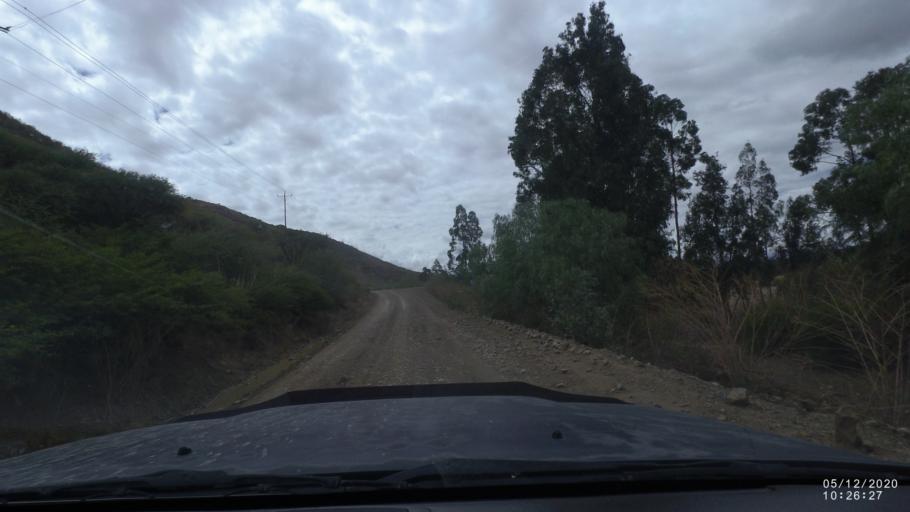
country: BO
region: Cochabamba
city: Sipe Sipe
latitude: -17.5264
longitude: -66.2833
